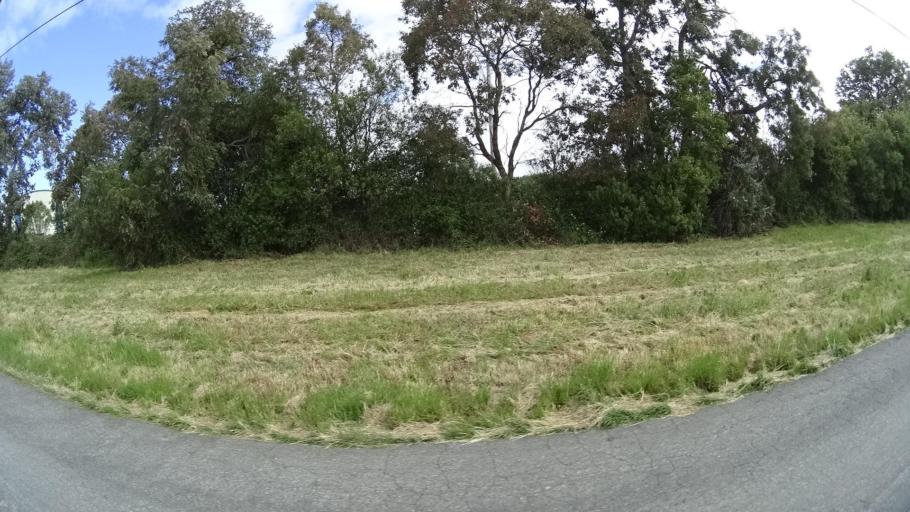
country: US
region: California
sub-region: Humboldt County
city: Arcata
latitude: 40.8824
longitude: -124.1054
